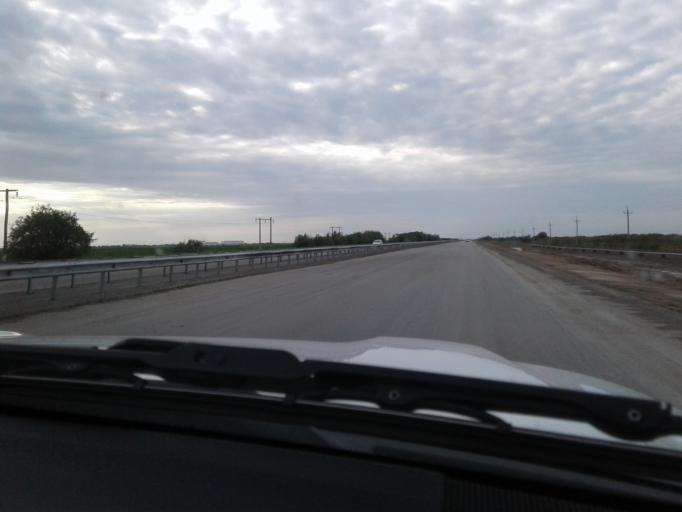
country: TM
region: Ahal
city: Tejen
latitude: 37.3420
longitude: 60.5800
